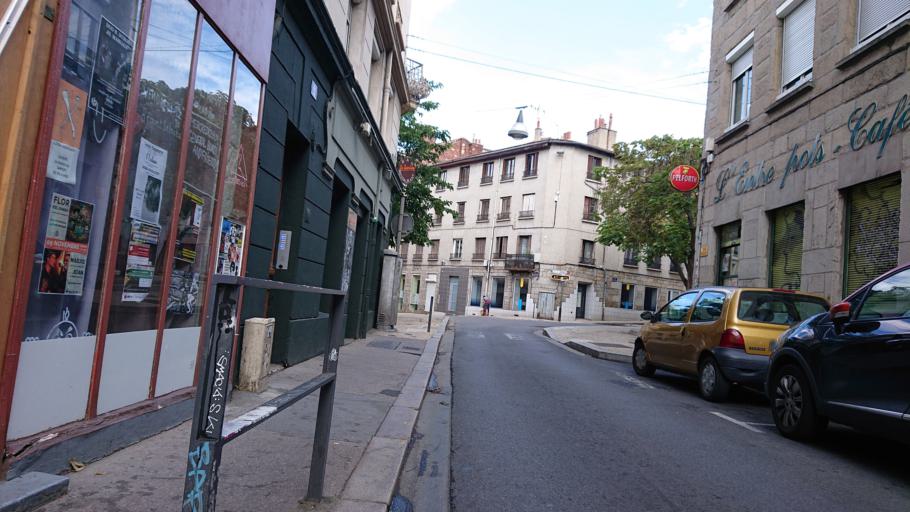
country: FR
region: Rhone-Alpes
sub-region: Departement de la Loire
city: Saint-Etienne
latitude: 45.4398
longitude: 4.3911
